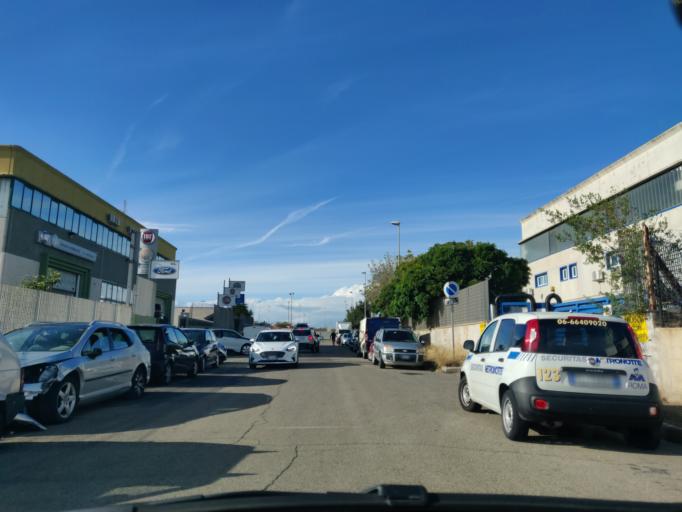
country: IT
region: Latium
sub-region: Citta metropolitana di Roma Capitale
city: Aurelia
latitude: 42.1191
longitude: 11.7828
